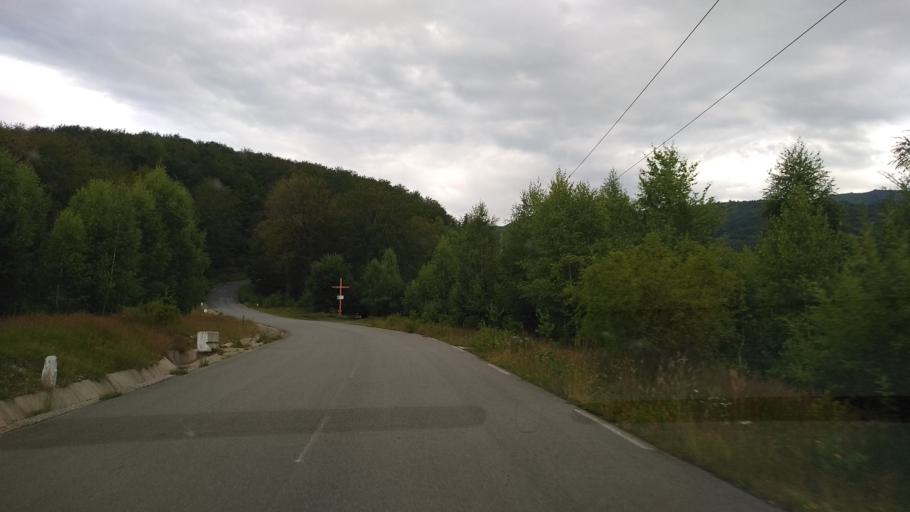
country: RO
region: Hunedoara
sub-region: Municipiul  Vulcan
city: Jiu-Paroseni
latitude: 45.3493
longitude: 23.2901
